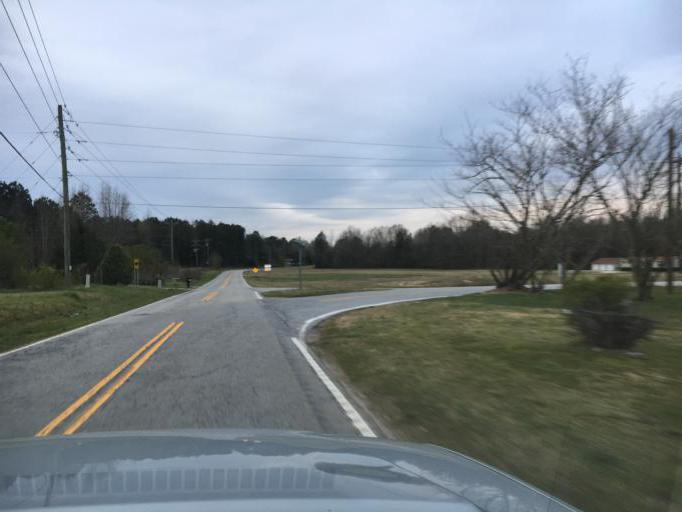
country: US
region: South Carolina
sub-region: Laurens County
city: Laurens
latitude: 34.5347
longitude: -82.0920
